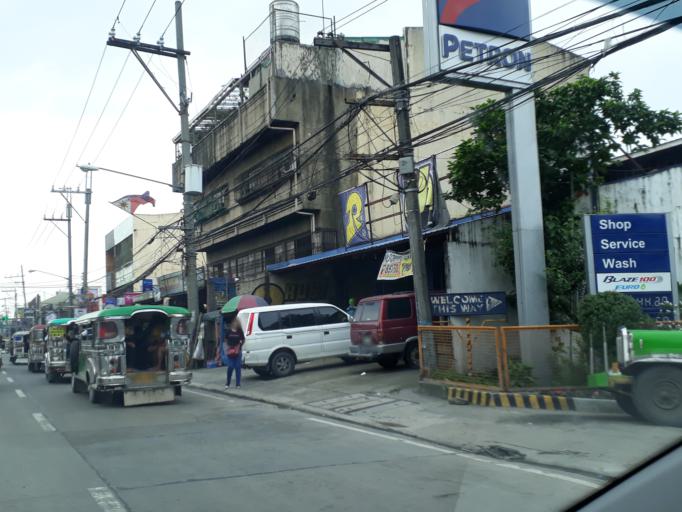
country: PH
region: Calabarzon
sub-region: Province of Rizal
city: Valenzuela
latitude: 14.7103
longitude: 120.9594
